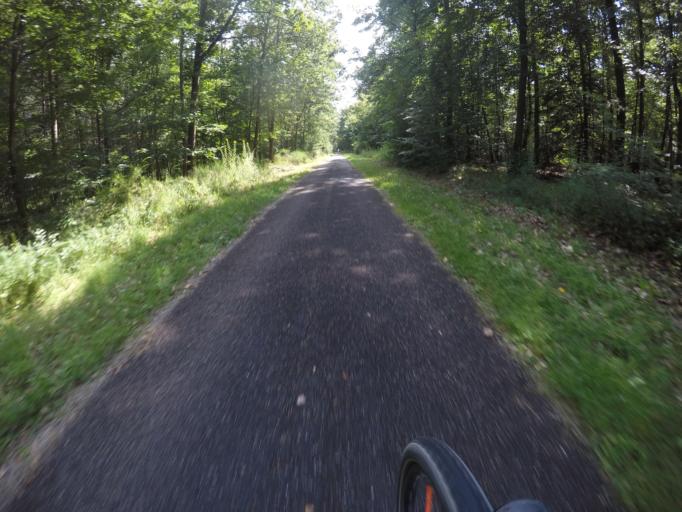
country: DE
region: Baden-Wuerttemberg
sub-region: Karlsruhe Region
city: Hambrucken
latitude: 49.2175
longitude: 8.5730
